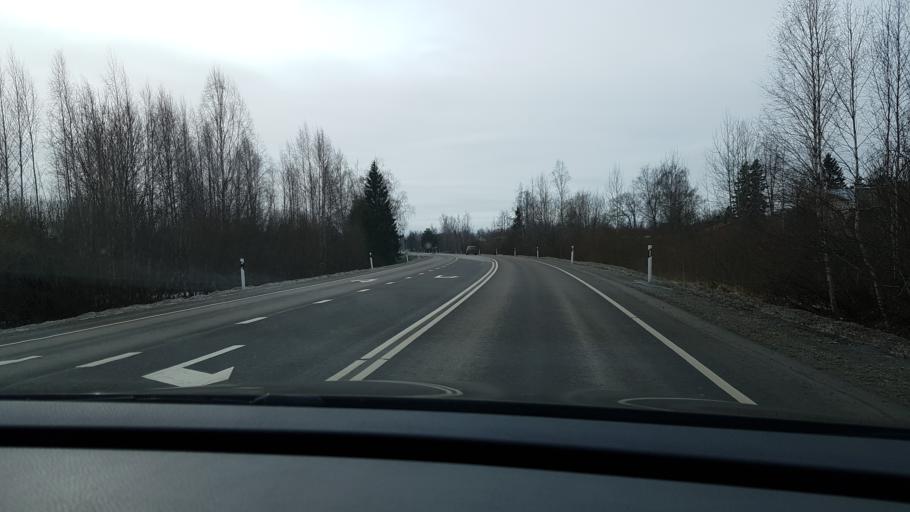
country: EE
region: Paernumaa
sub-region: Sindi linn
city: Sindi
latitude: 58.4008
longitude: 24.6516
